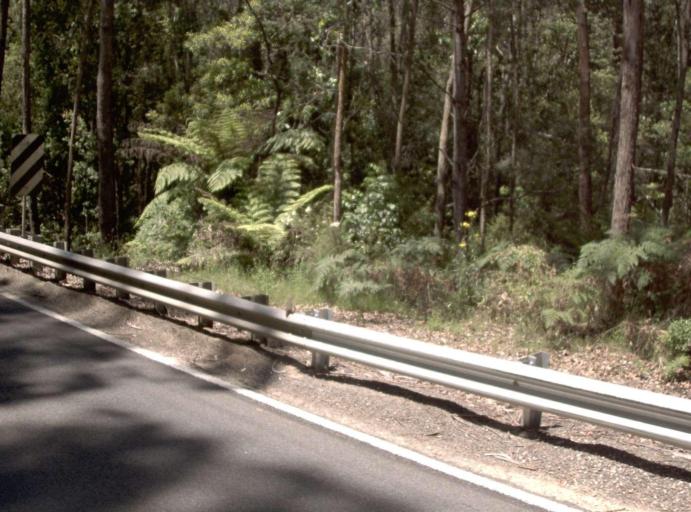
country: AU
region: New South Wales
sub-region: Bombala
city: Bombala
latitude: -37.5911
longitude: 148.9184
